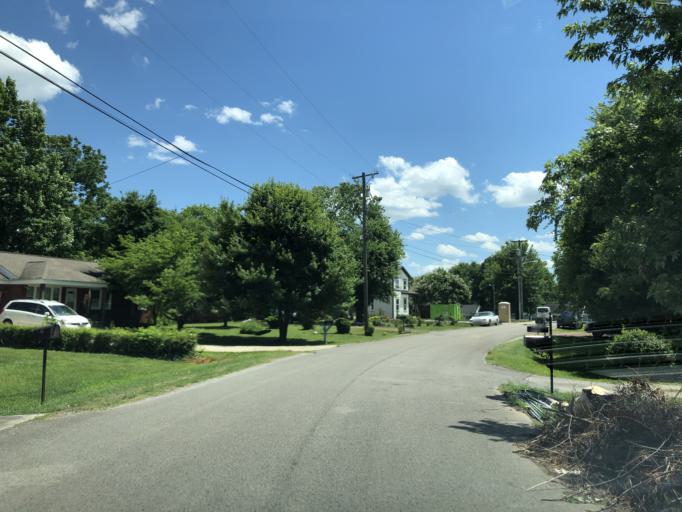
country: US
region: Tennessee
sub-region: Davidson County
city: Nashville
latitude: 36.1857
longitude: -86.7222
